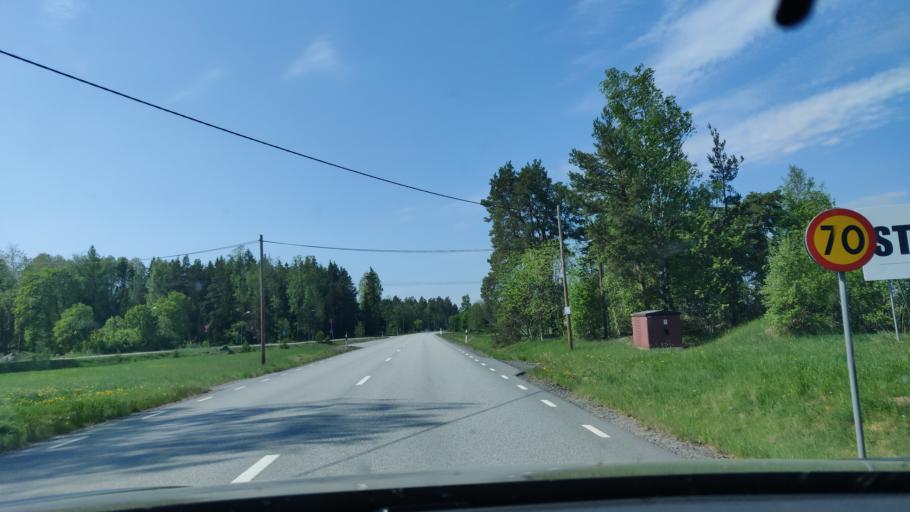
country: SE
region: Uppsala
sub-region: Heby Kommun
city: OEstervala
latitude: 60.1652
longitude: 17.1957
